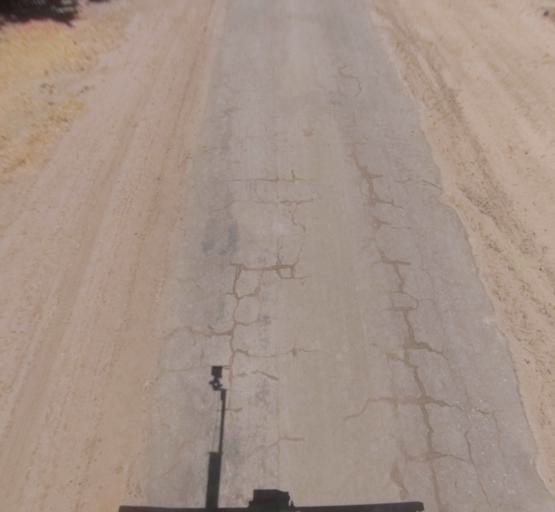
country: US
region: California
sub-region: Madera County
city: Fairmead
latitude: 37.0329
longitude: -120.2170
